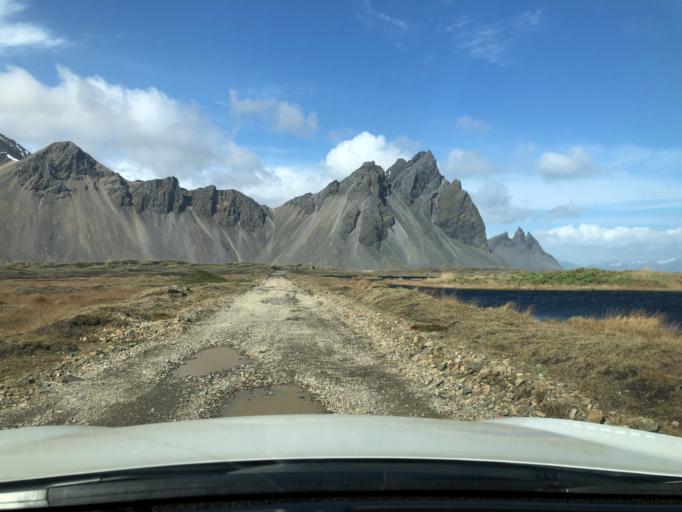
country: IS
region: East
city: Hoefn
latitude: 64.2419
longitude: -14.9717
